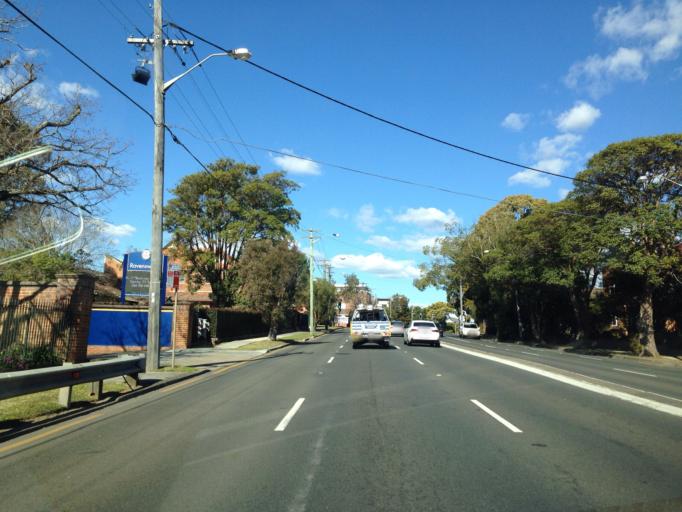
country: AU
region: New South Wales
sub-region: Ku-ring-gai
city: Killara
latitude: -33.7596
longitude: 151.1543
